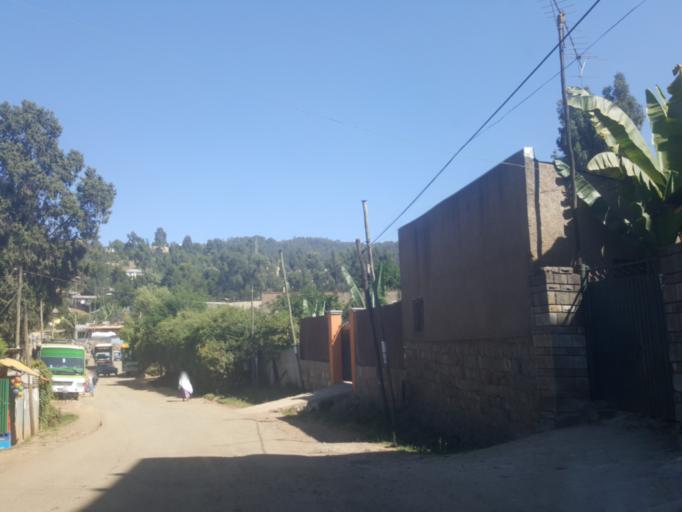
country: ET
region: Adis Abeba
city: Addis Ababa
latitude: 9.0678
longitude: 38.7329
